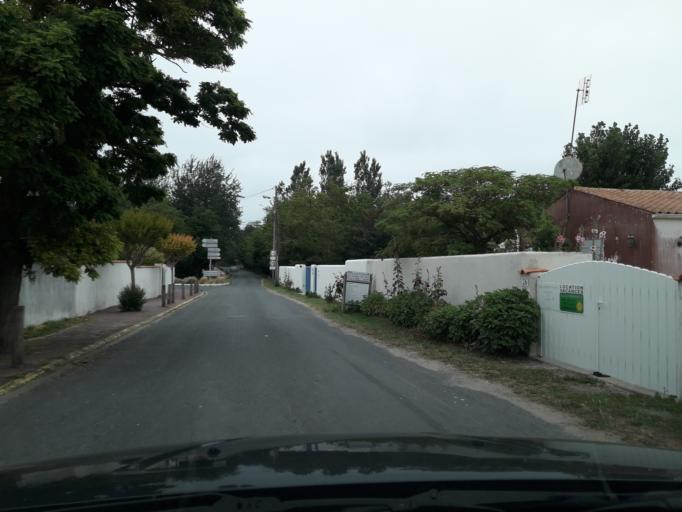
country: FR
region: Poitou-Charentes
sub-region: Departement de la Charente-Maritime
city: Boyard-Ville
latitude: 45.9692
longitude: -1.2382
